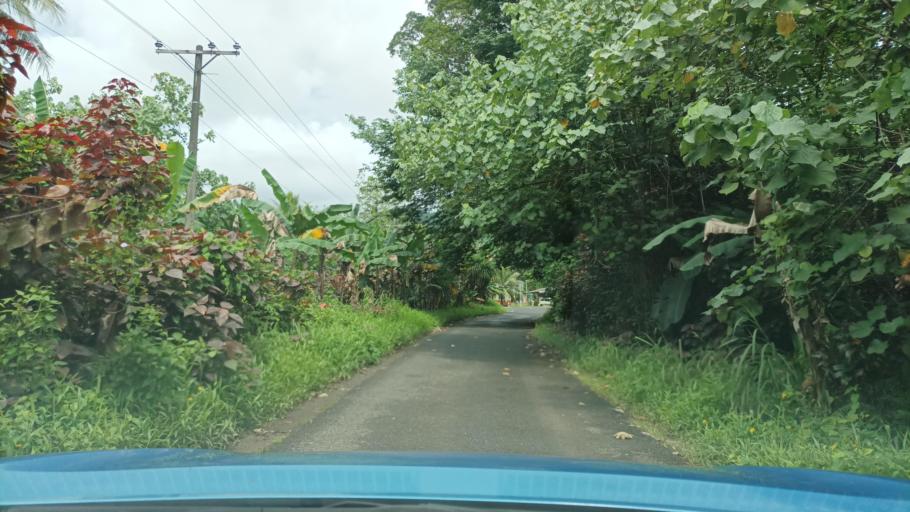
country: FM
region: Pohnpei
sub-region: Madolenihm Municipality
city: Madolenihm Municipality Government
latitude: 6.8889
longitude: 158.3145
